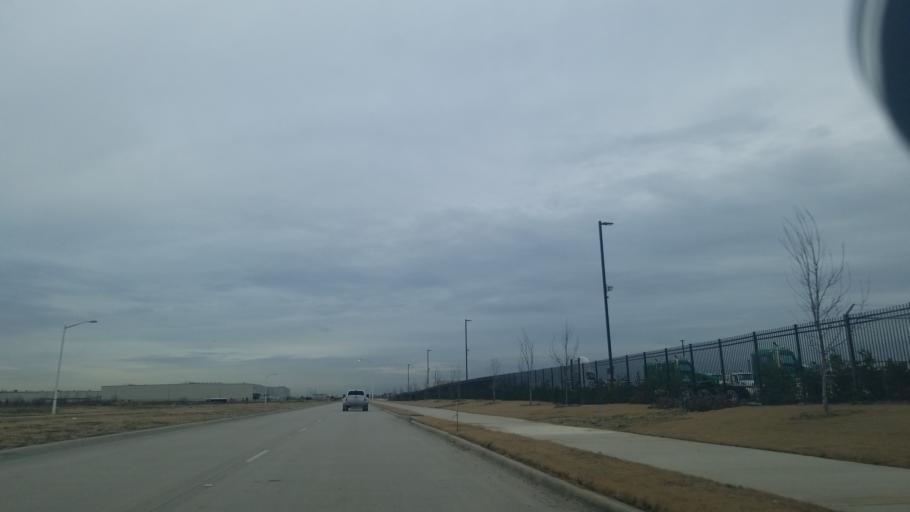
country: US
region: Texas
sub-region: Denton County
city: Denton
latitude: 33.2051
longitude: -97.1849
